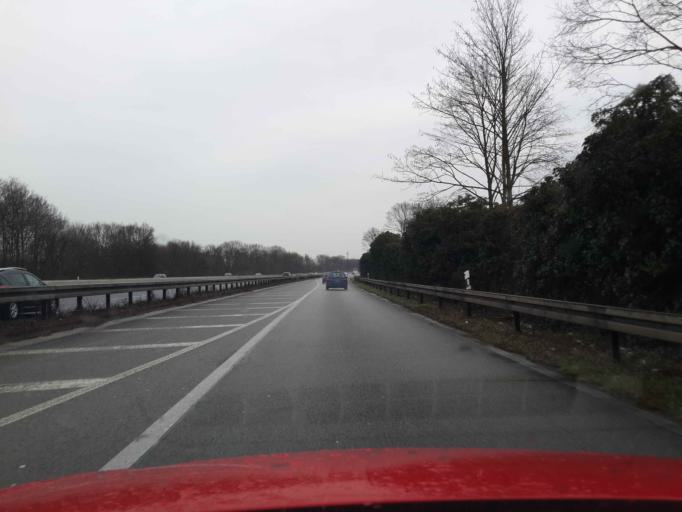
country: DE
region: North Rhine-Westphalia
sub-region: Regierungsbezirk Dusseldorf
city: Ratingen
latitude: 51.3548
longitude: 6.8646
